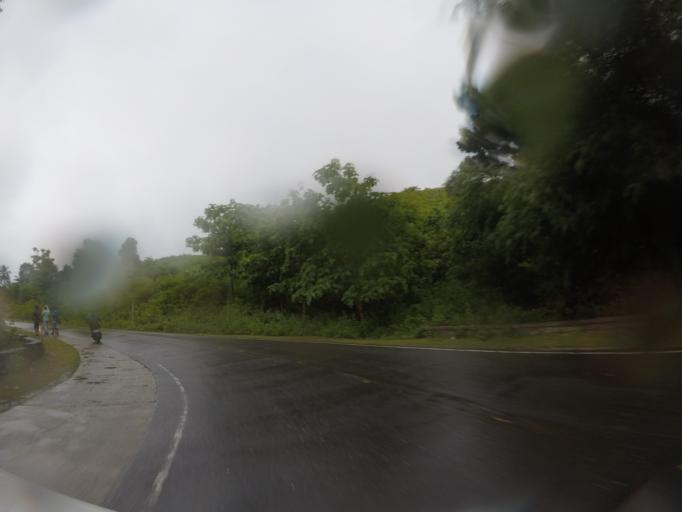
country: TL
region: Bobonaro
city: Maliana
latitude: -8.9674
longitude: 125.0521
